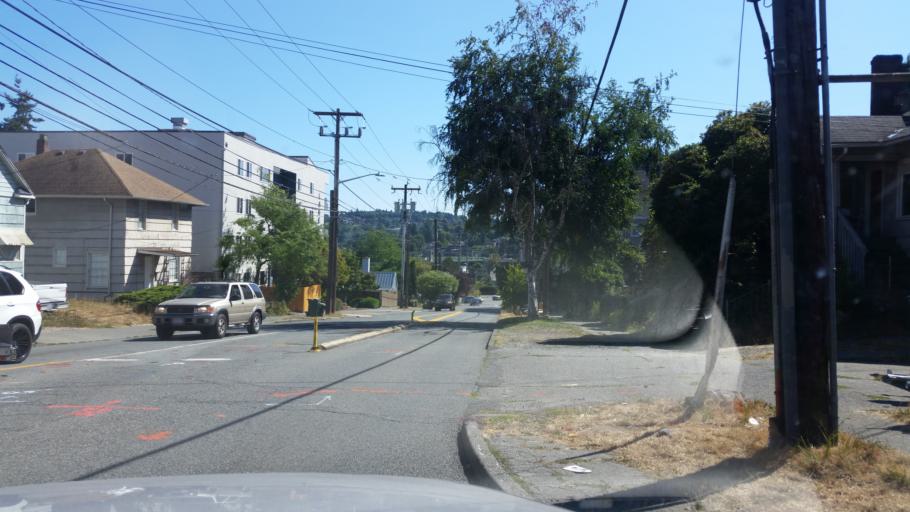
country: US
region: Washington
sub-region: King County
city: Seattle
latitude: 47.6574
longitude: -122.3209
